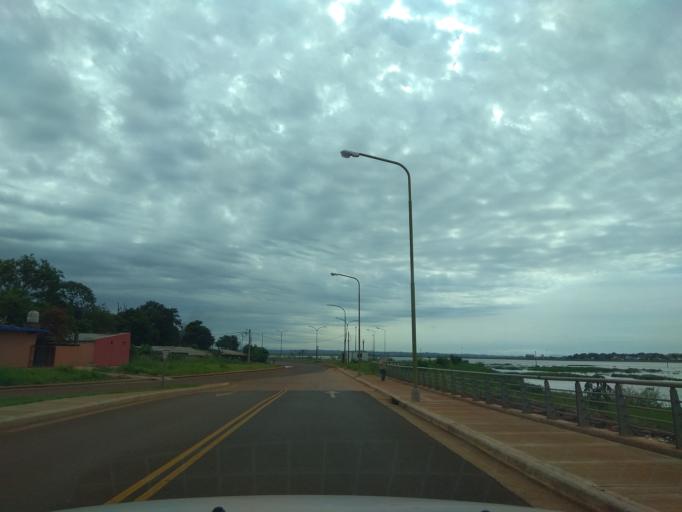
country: AR
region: Misiones
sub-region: Departamento de Capital
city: Posadas
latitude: -27.4175
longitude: -55.8994
